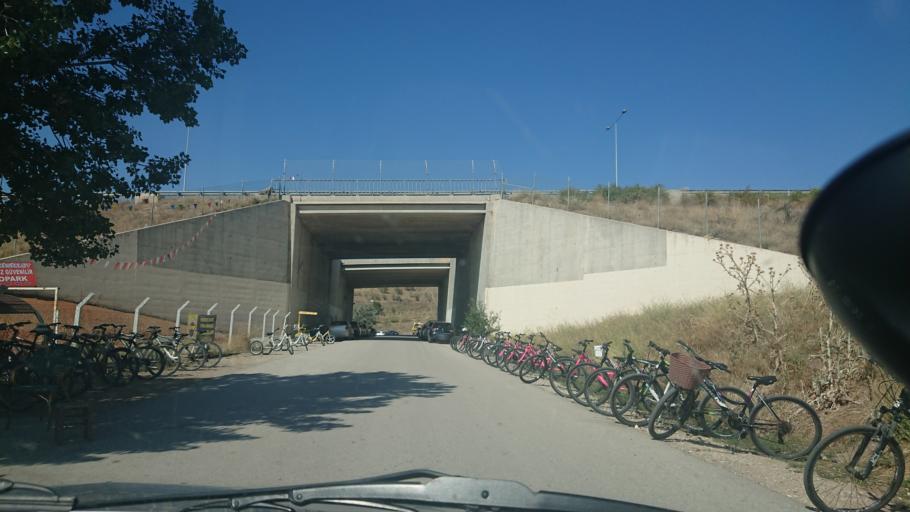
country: TR
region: Ankara
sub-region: Goelbasi
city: Golbasi
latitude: 39.8122
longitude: 32.8219
